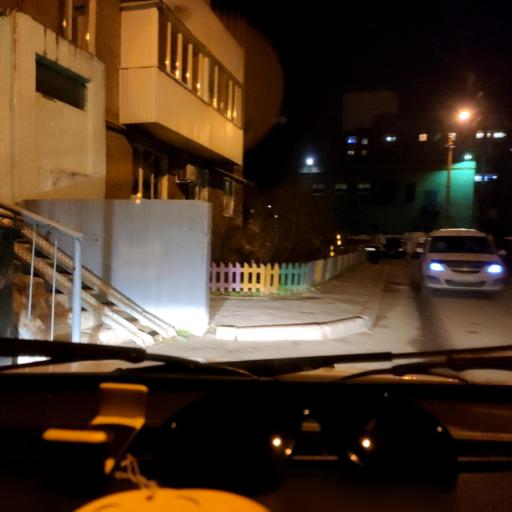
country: RU
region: Bashkortostan
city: Ufa
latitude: 54.7752
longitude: 56.1197
